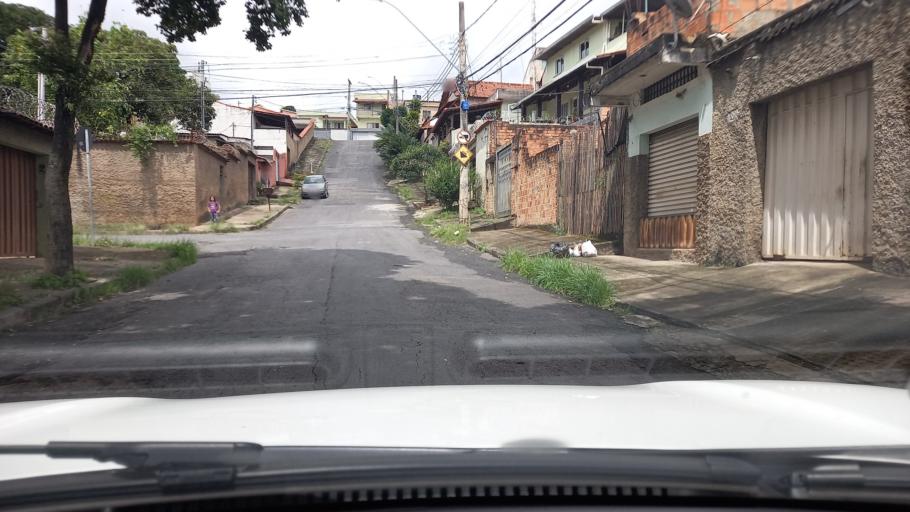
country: BR
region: Minas Gerais
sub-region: Contagem
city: Contagem
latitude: -19.8989
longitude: -44.0120
